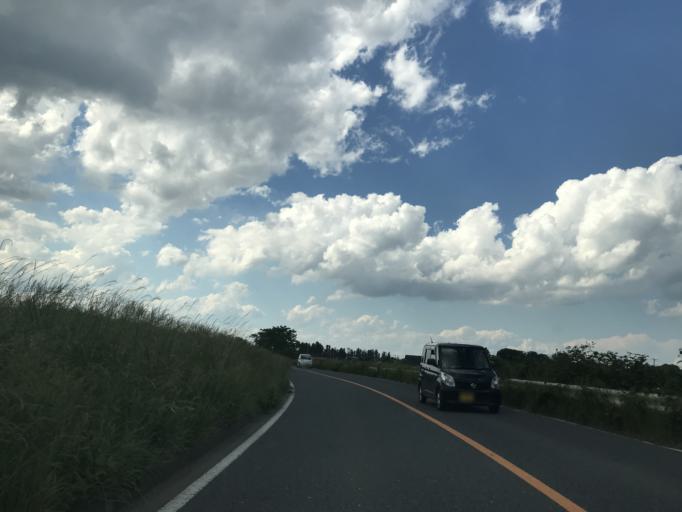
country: JP
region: Miyagi
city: Wakuya
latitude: 38.6644
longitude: 141.2150
